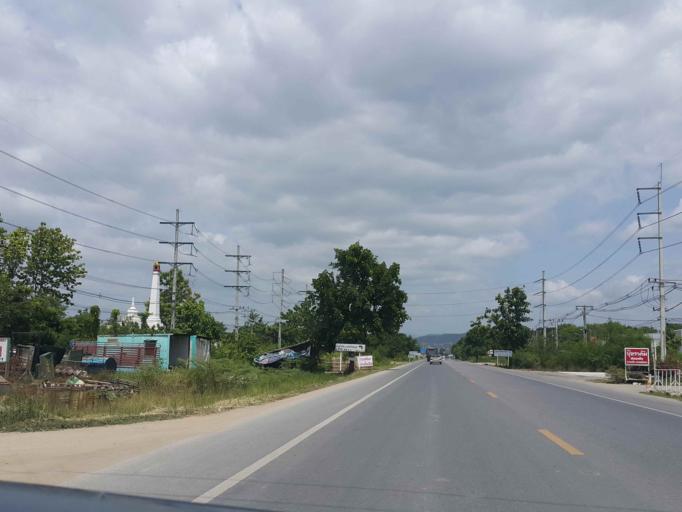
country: TH
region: Chiang Mai
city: Hang Dong
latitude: 18.7222
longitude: 98.9524
